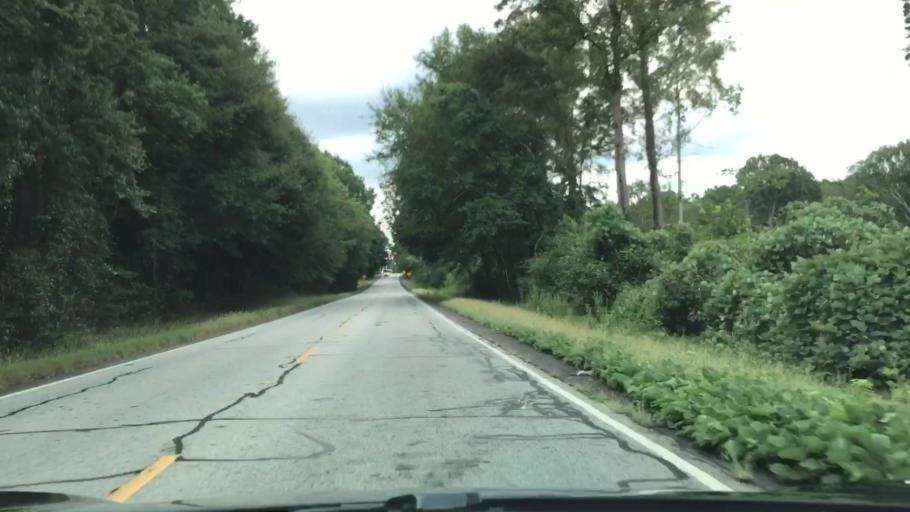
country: US
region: Georgia
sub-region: Barrow County
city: Russell
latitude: 33.9584
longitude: -83.6614
